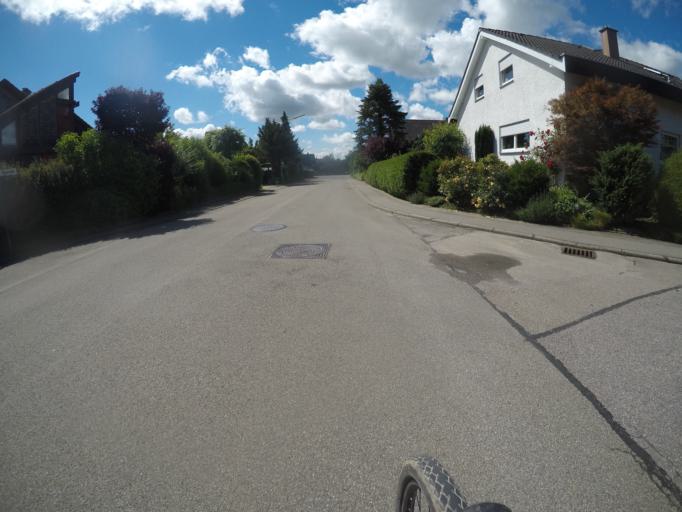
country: DE
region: Baden-Wuerttemberg
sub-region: Regierungsbezirk Stuttgart
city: Unterjettingen
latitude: 48.5618
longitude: 8.7858
